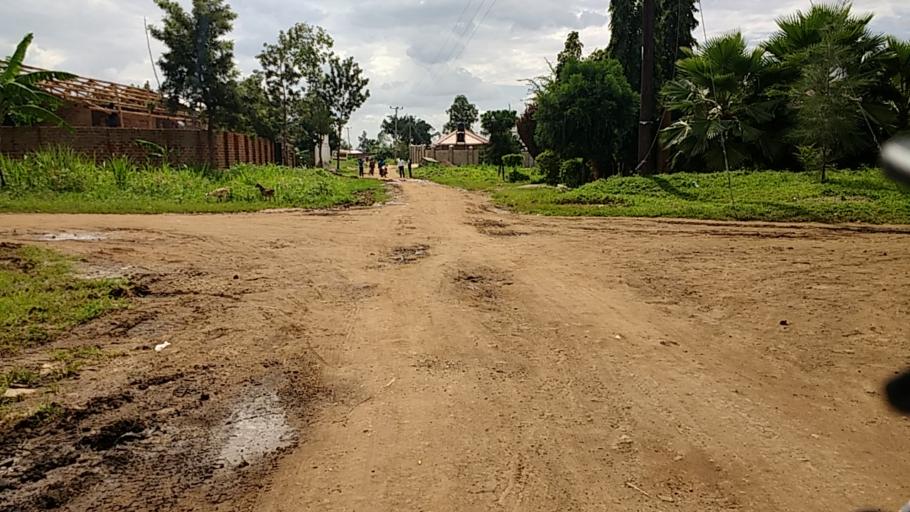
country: UG
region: Eastern Region
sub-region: Mbale District
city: Mbale
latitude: 1.0882
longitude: 34.1720
